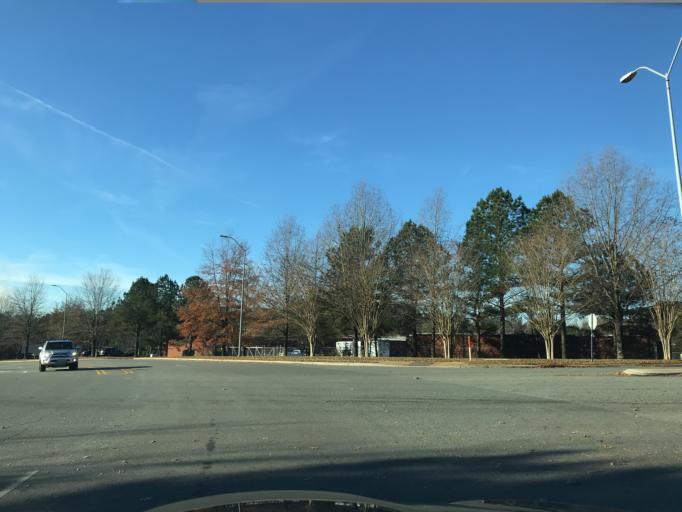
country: US
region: North Carolina
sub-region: Wake County
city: Morrisville
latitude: 35.9051
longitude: -78.7486
